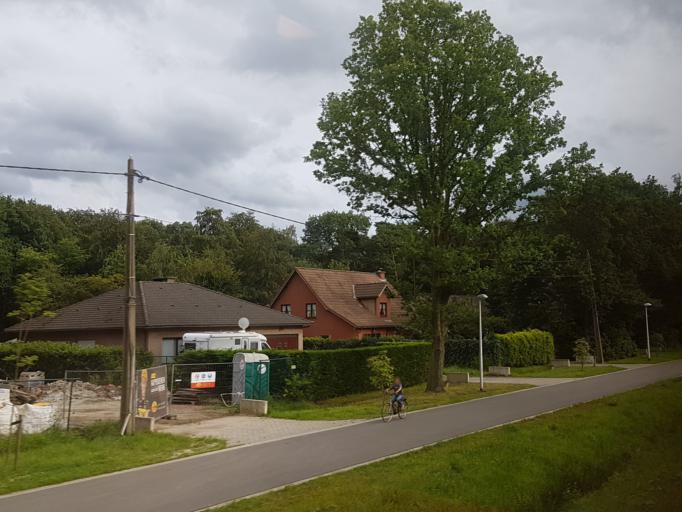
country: BE
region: Flanders
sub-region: Provincie Antwerpen
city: Kapellen
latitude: 51.3303
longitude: 4.4419
